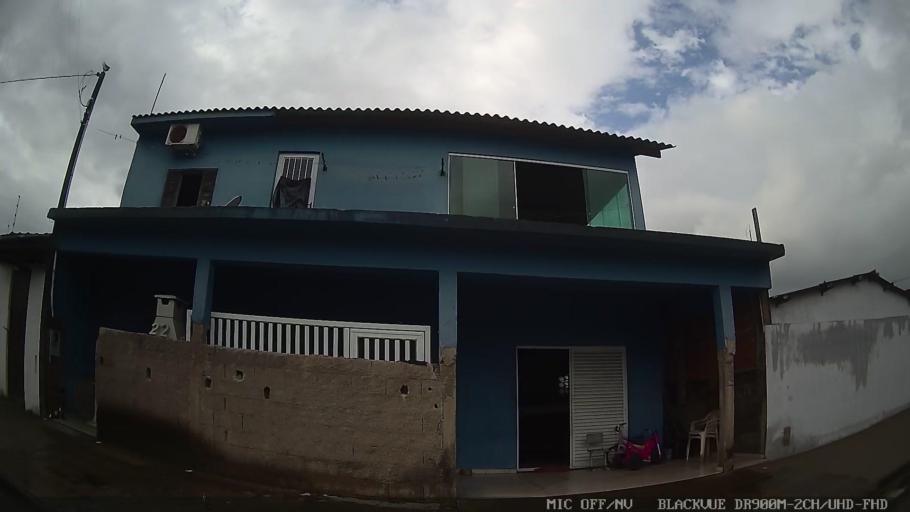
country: BR
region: Sao Paulo
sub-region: Itanhaem
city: Itanhaem
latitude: -24.1900
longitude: -46.8135
